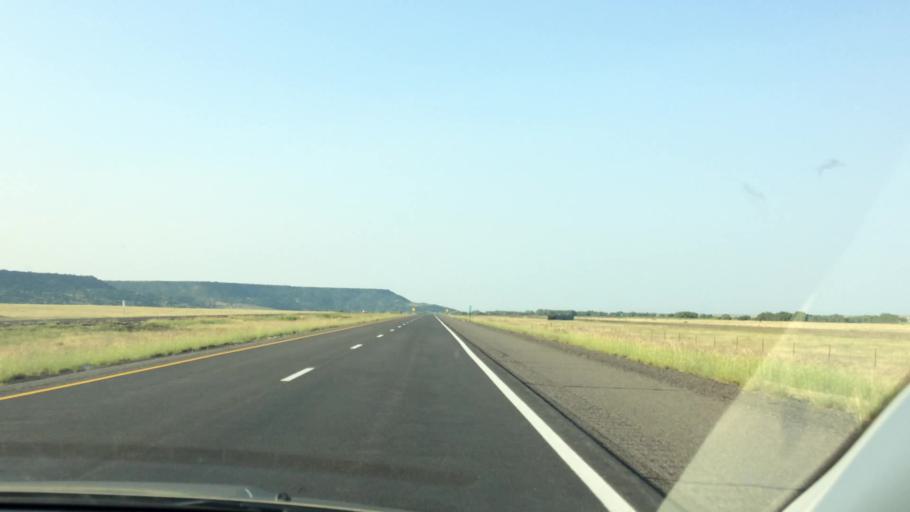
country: US
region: New Mexico
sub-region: Colfax County
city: Raton
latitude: 36.7368
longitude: -104.4565
